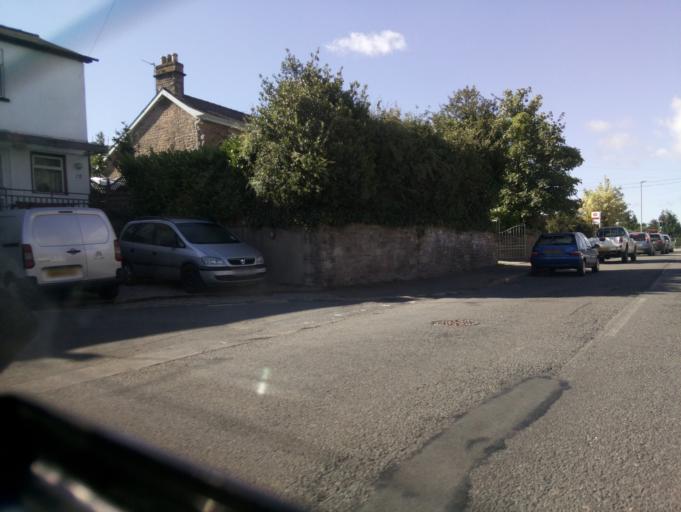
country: GB
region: England
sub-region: Herefordshire
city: Walford
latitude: 51.9040
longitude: -2.5879
